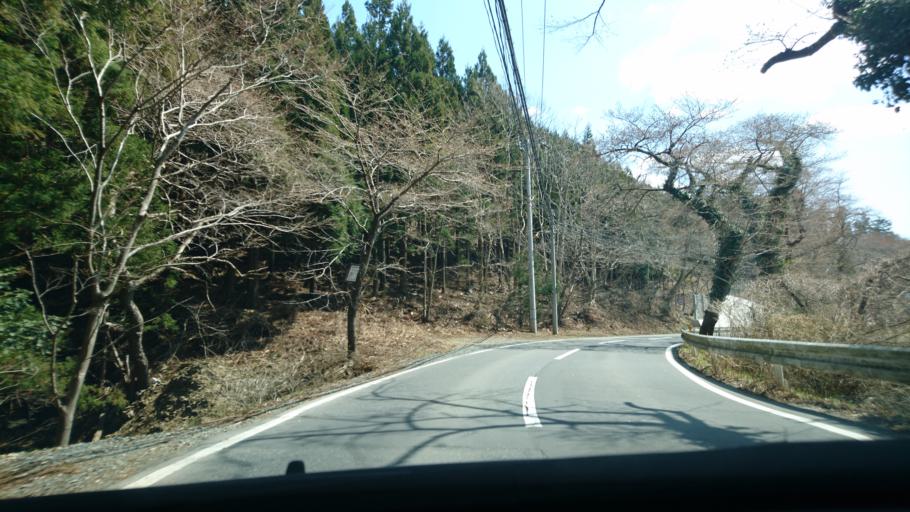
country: JP
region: Miyagi
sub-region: Oshika Gun
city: Onagawa Cho
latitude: 38.4454
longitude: 141.4777
